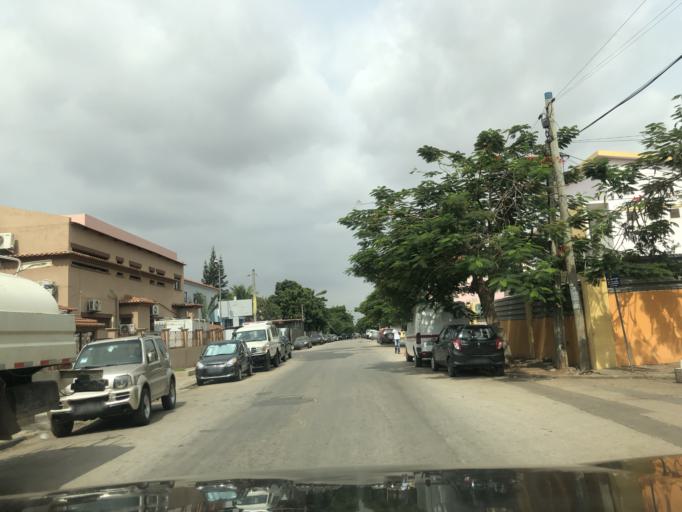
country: AO
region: Luanda
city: Luanda
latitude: -8.8290
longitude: 13.2487
